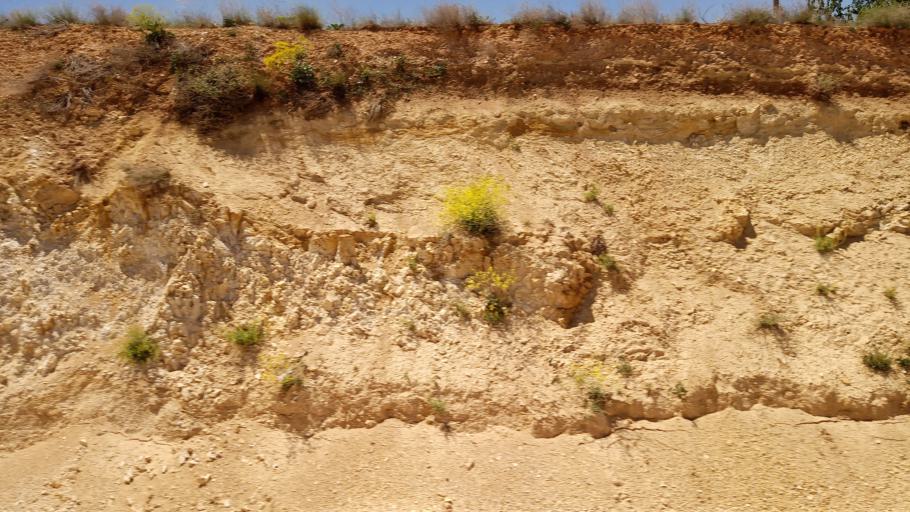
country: TR
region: Malatya
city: Darende
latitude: 38.6336
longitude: 37.4543
